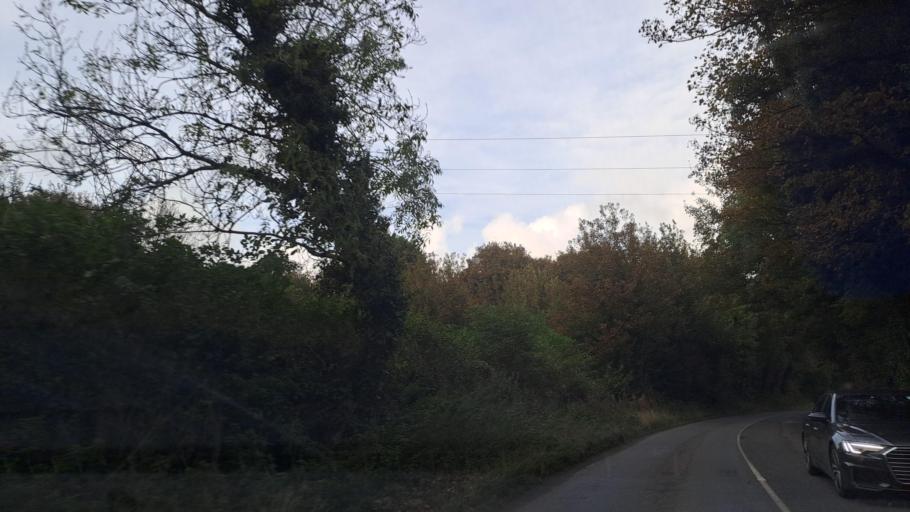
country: IE
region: Ulster
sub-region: An Cabhan
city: Kingscourt
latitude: 53.8789
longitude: -6.8056
